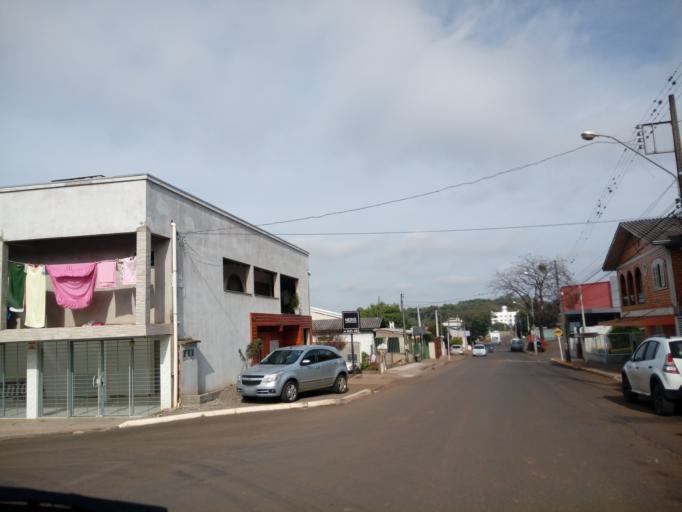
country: BR
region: Santa Catarina
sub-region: Chapeco
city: Chapeco
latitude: -27.1009
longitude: -52.6400
